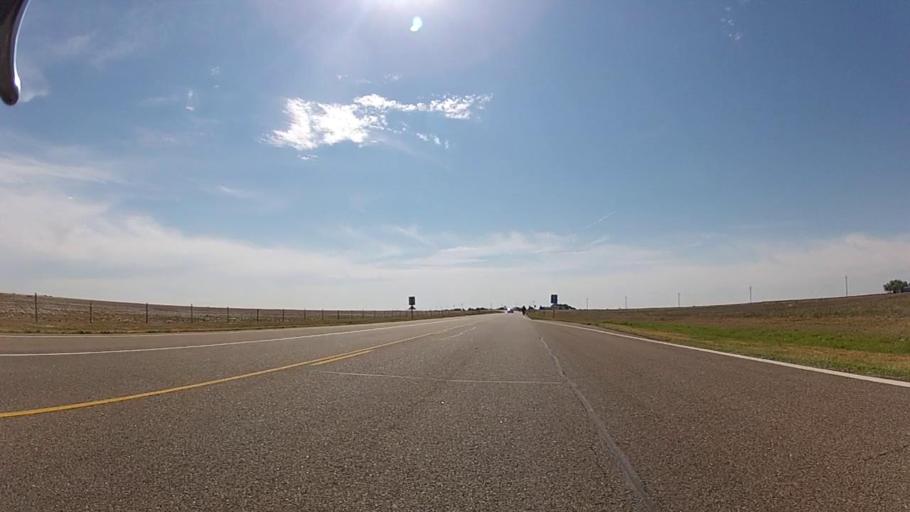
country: US
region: Kansas
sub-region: Grant County
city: Ulysses
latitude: 37.5635
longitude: -101.3075
